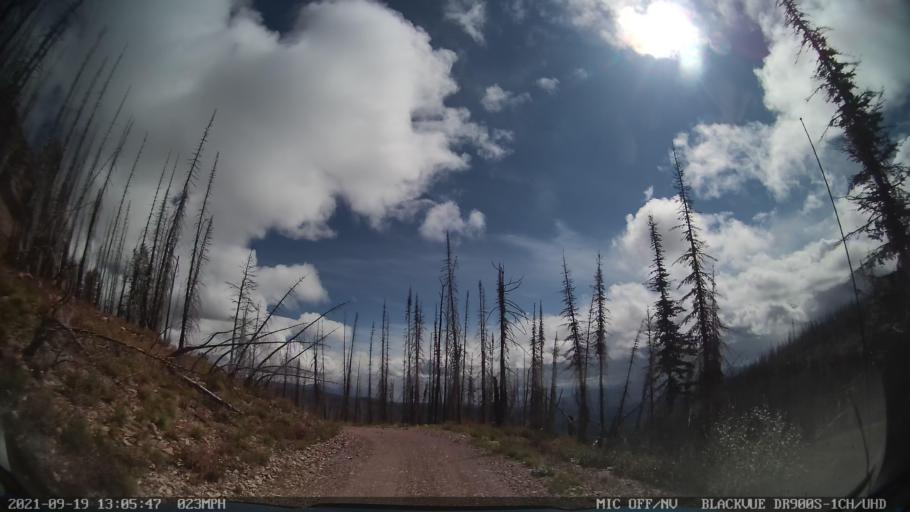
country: US
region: Montana
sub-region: Missoula County
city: Seeley Lake
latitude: 47.1905
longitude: -113.3501
